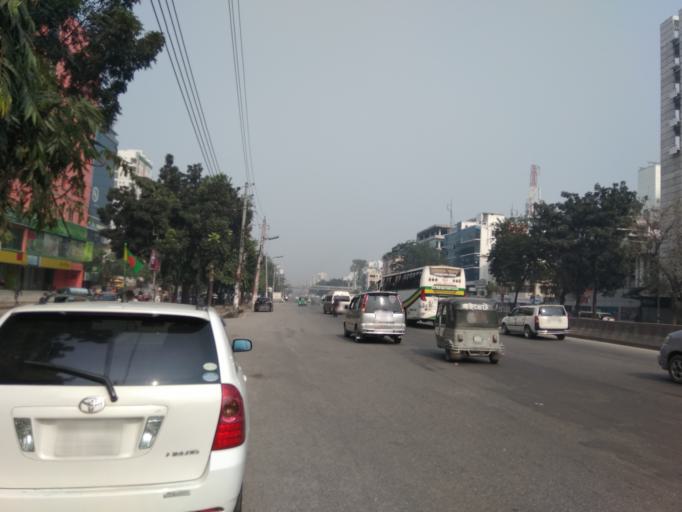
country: BD
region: Dhaka
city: Tungi
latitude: 23.8623
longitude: 90.3999
